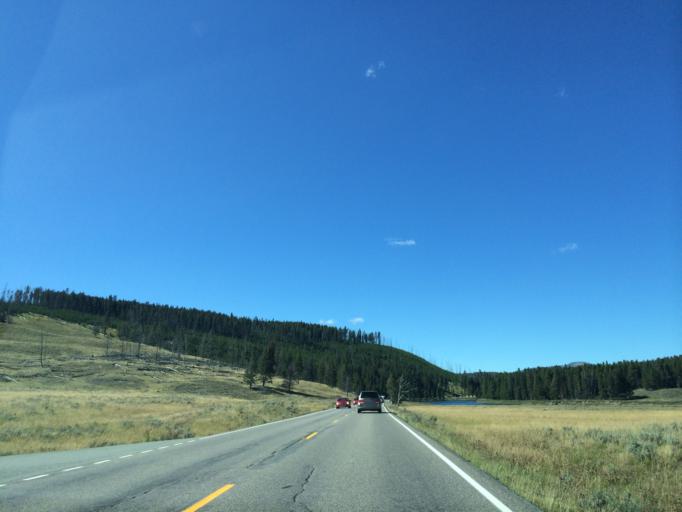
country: US
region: Montana
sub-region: Gallatin County
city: West Yellowstone
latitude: 44.6812
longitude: -110.4910
